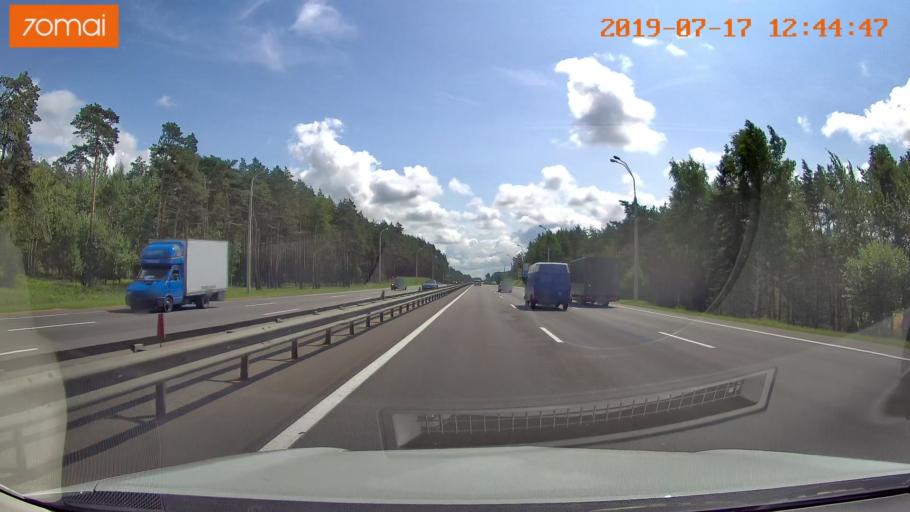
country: BY
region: Minsk
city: Vyaliki Trastsyanets
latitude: 53.8290
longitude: 27.7448
